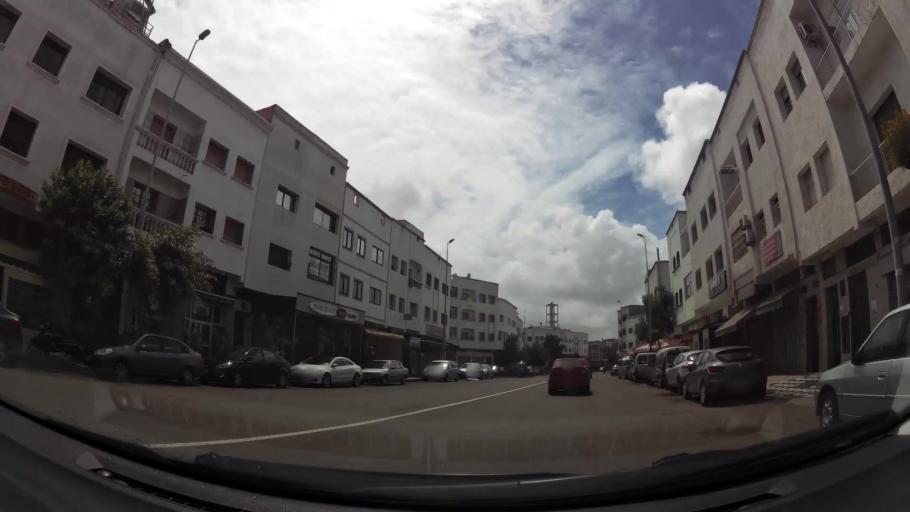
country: MA
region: Grand Casablanca
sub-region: Casablanca
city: Casablanca
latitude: 33.5467
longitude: -7.6817
